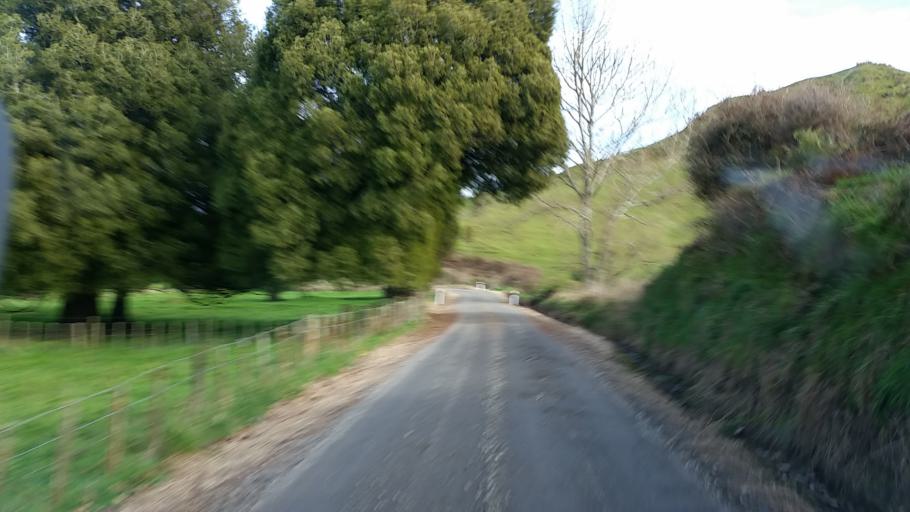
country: NZ
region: Taranaki
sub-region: South Taranaki District
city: Eltham
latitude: -39.2555
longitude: 174.5277
